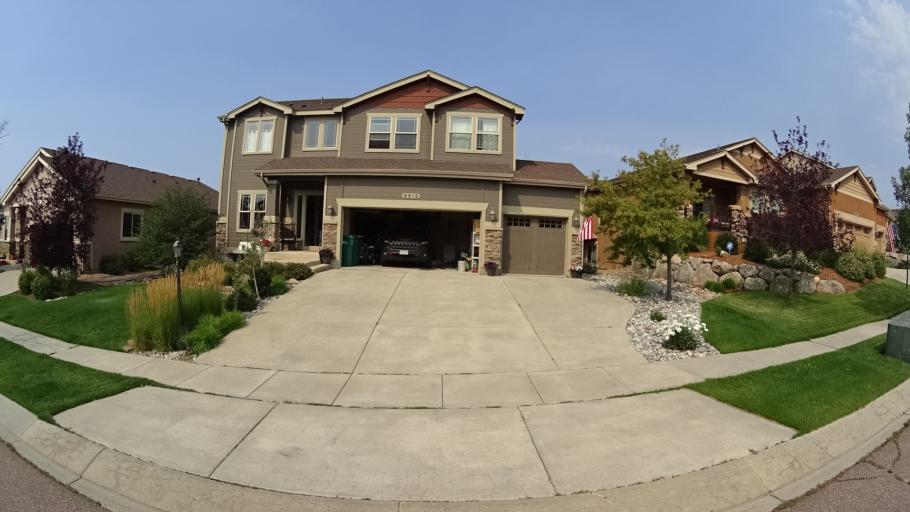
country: US
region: Colorado
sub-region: El Paso County
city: Black Forest
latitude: 38.9694
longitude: -104.7341
